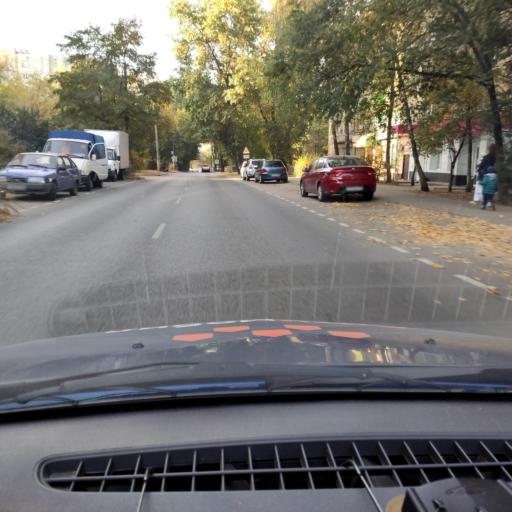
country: RU
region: Voronezj
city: Voronezh
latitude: 51.6756
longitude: 39.1522
